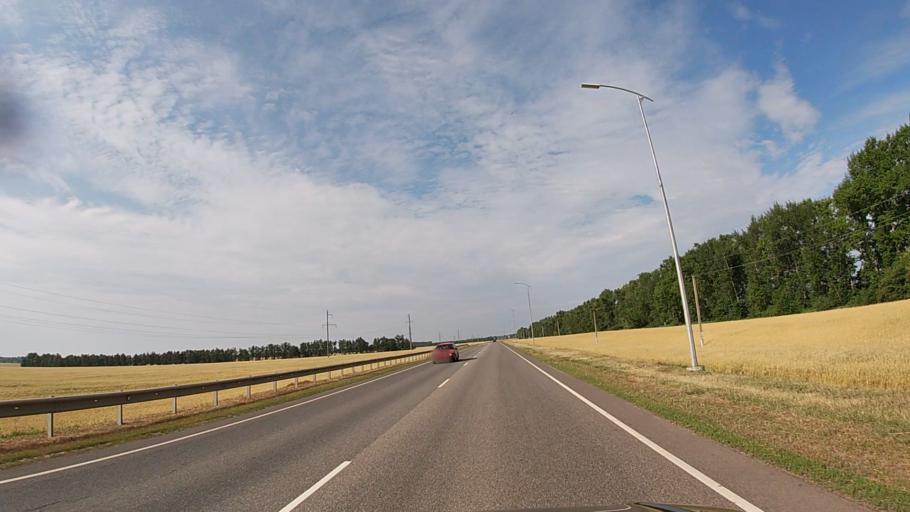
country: RU
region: Belgorod
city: Proletarskiy
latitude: 50.8166
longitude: 35.7528
